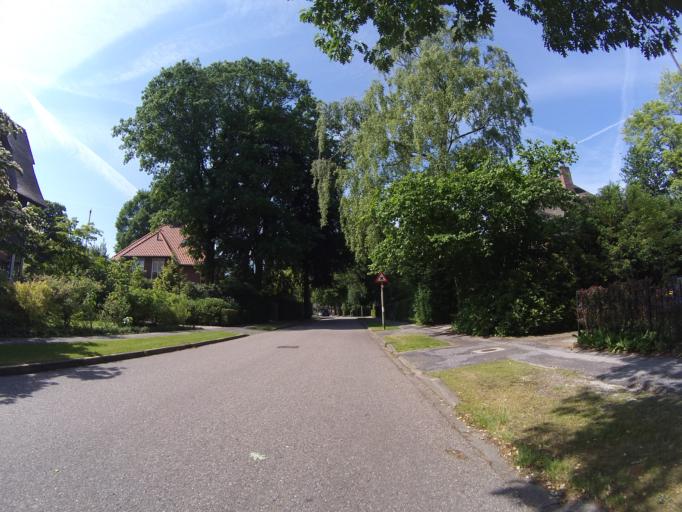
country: NL
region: Utrecht
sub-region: Gemeente Amersfoort
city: Amersfoort
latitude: 52.1514
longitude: 5.3701
